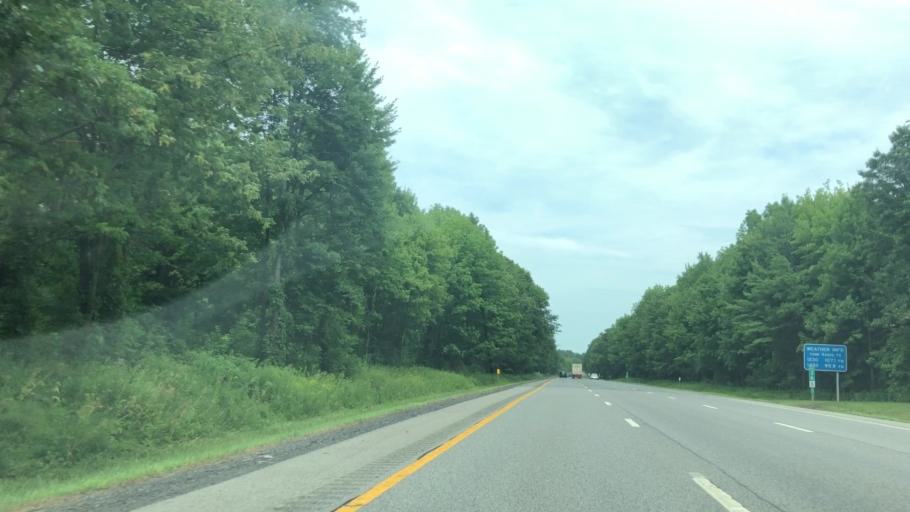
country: US
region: New York
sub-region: Saratoga County
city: Saratoga Springs
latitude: 43.1768
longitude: -73.7091
